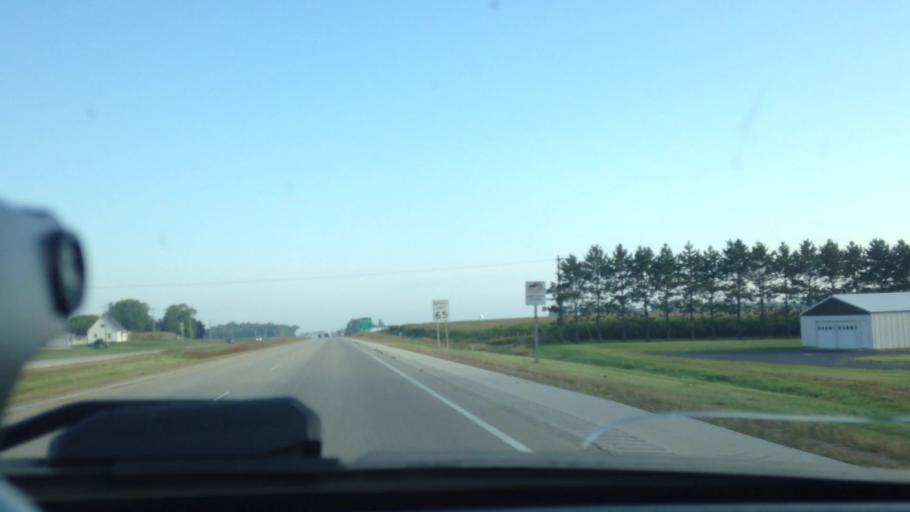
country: US
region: Wisconsin
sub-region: Oconto County
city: Oconto Falls
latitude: 45.0373
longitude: -88.0444
